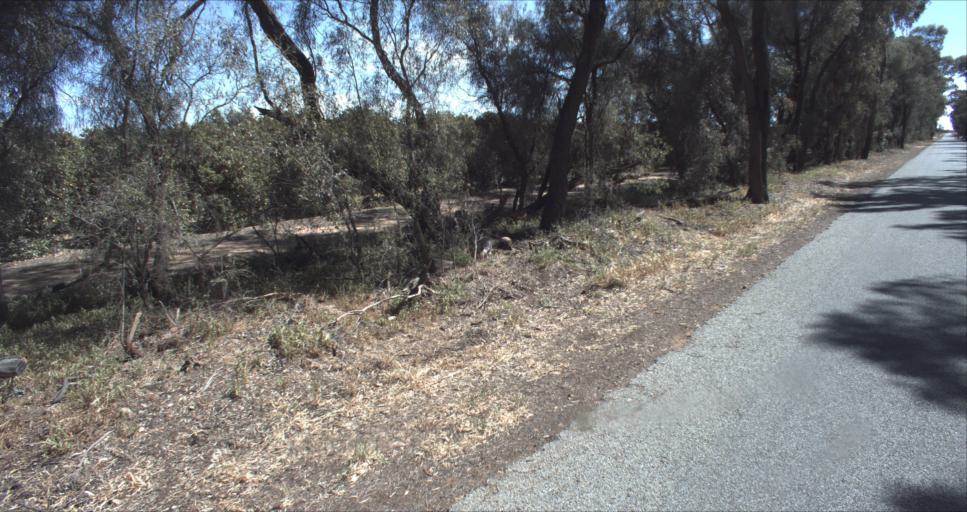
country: AU
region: New South Wales
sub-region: Leeton
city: Leeton
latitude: -34.5322
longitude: 146.3418
